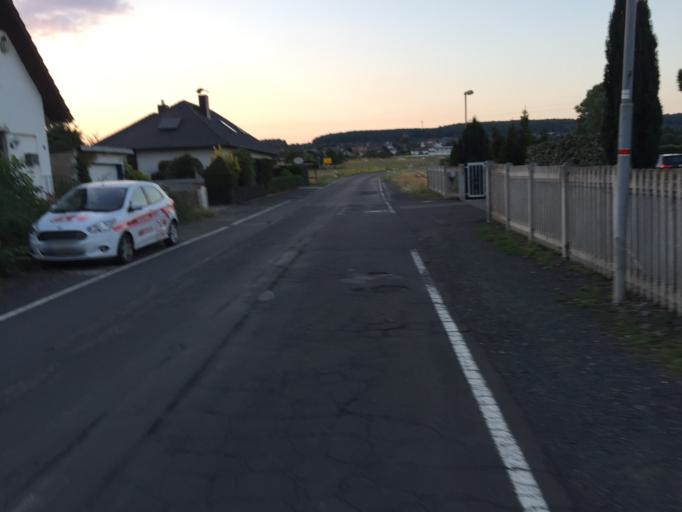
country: DE
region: Hesse
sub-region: Regierungsbezirk Giessen
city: Alten Buseck
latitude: 50.6115
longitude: 8.7519
